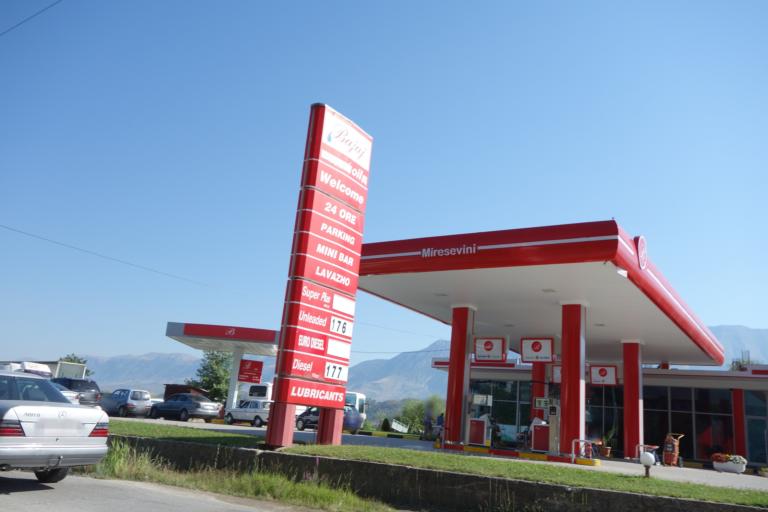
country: AL
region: Gjirokaster
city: Gjirokaster
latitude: 40.0864
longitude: 20.1429
